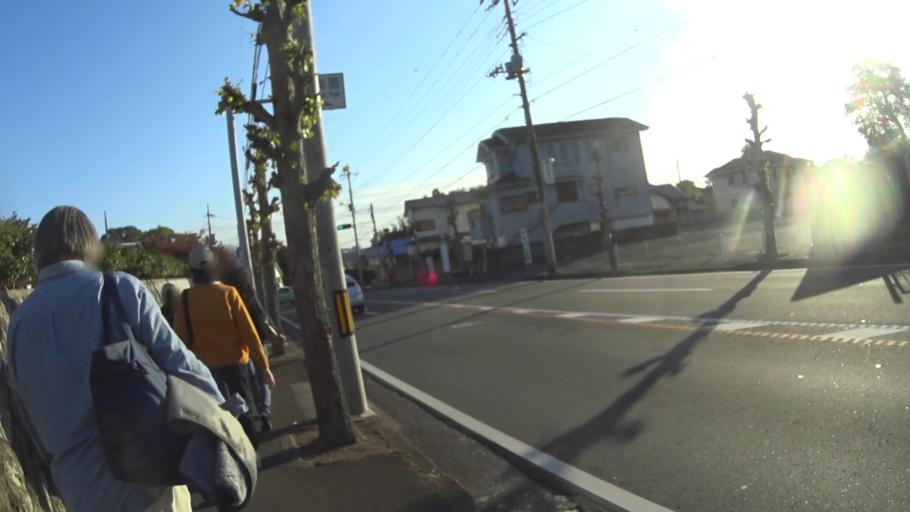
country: JP
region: Ibaraki
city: Mito-shi
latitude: 36.3762
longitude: 140.4592
